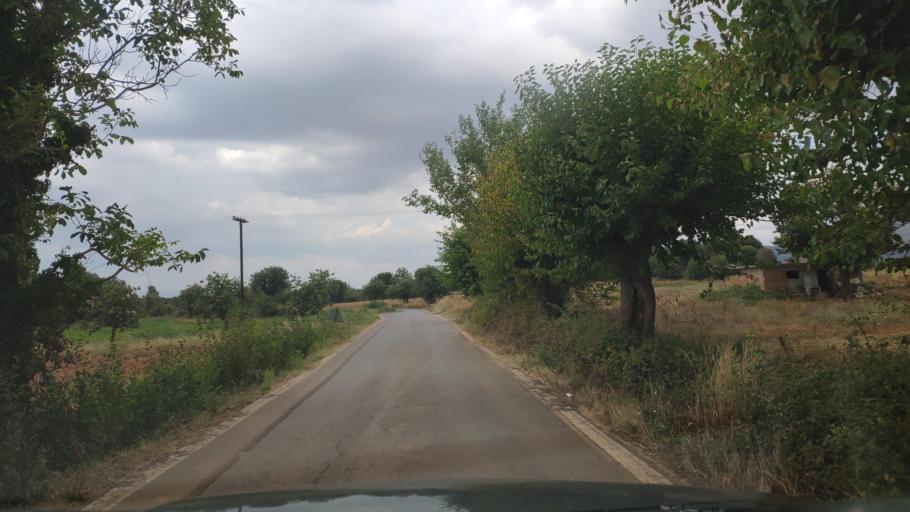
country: GR
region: Peloponnese
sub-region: Nomos Lakonias
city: Kariai
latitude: 37.3191
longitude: 22.4375
